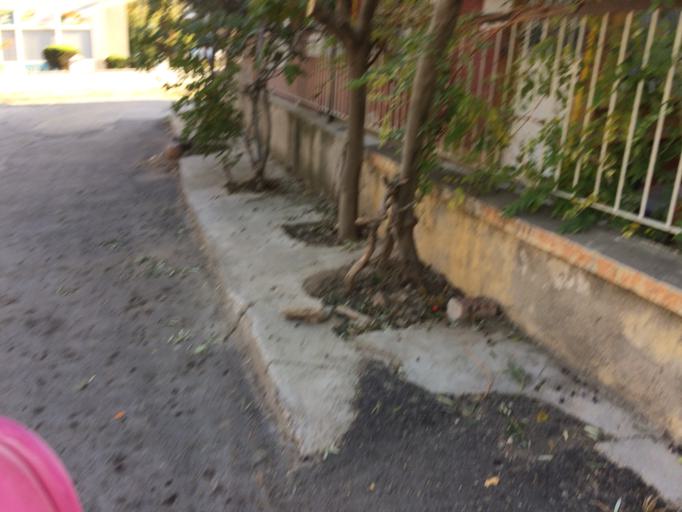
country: TR
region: Izmir
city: Karsiyaka
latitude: 38.4906
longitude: 27.0610
